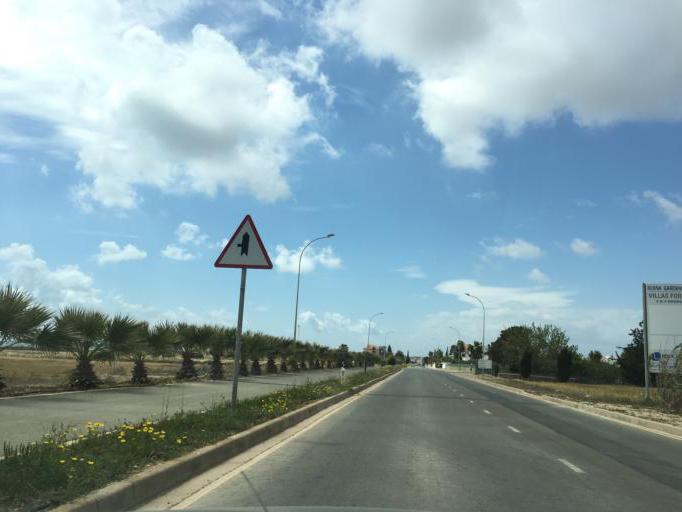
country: CY
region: Ammochostos
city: Liopetri
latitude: 34.9778
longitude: 33.9171
